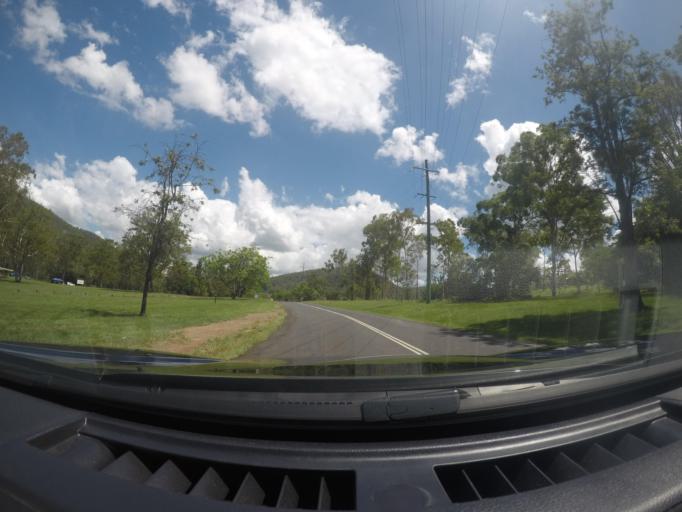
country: AU
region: Queensland
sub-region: Moreton Bay
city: Woodford
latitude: -27.1202
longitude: 152.5503
